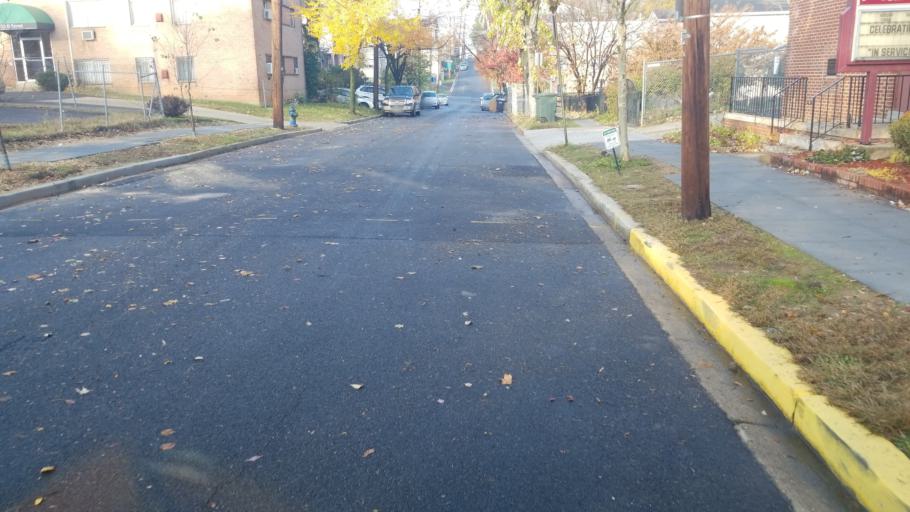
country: US
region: Maryland
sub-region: Prince George's County
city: Capitol Heights
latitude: 38.8862
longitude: -76.9268
